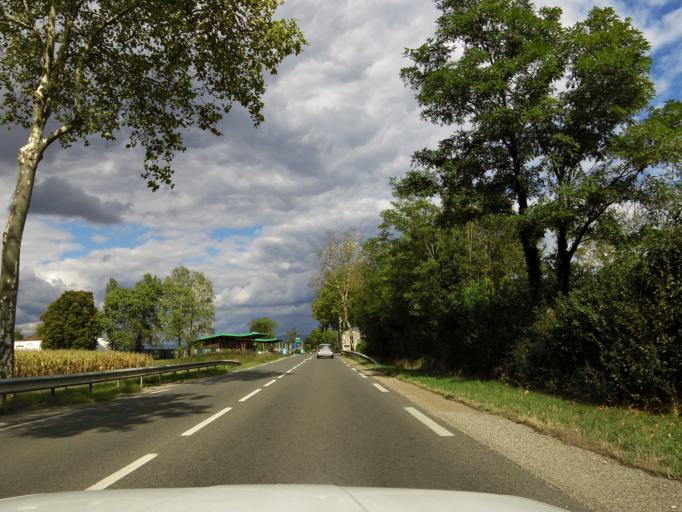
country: FR
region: Rhone-Alpes
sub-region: Departement de l'Ain
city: Leyment
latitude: 45.9208
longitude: 5.2676
